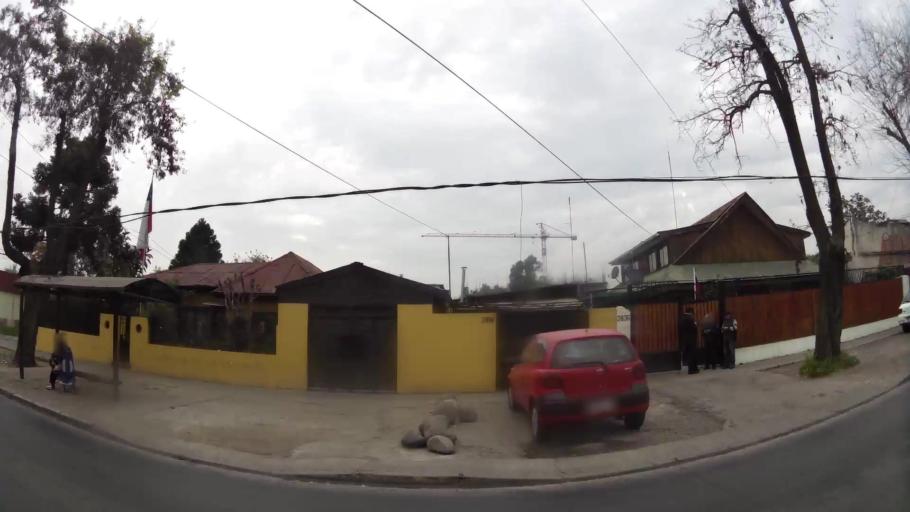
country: CL
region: Santiago Metropolitan
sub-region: Provincia de Santiago
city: Villa Presidente Frei, Nunoa, Santiago, Chile
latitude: -33.4739
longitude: -70.6023
